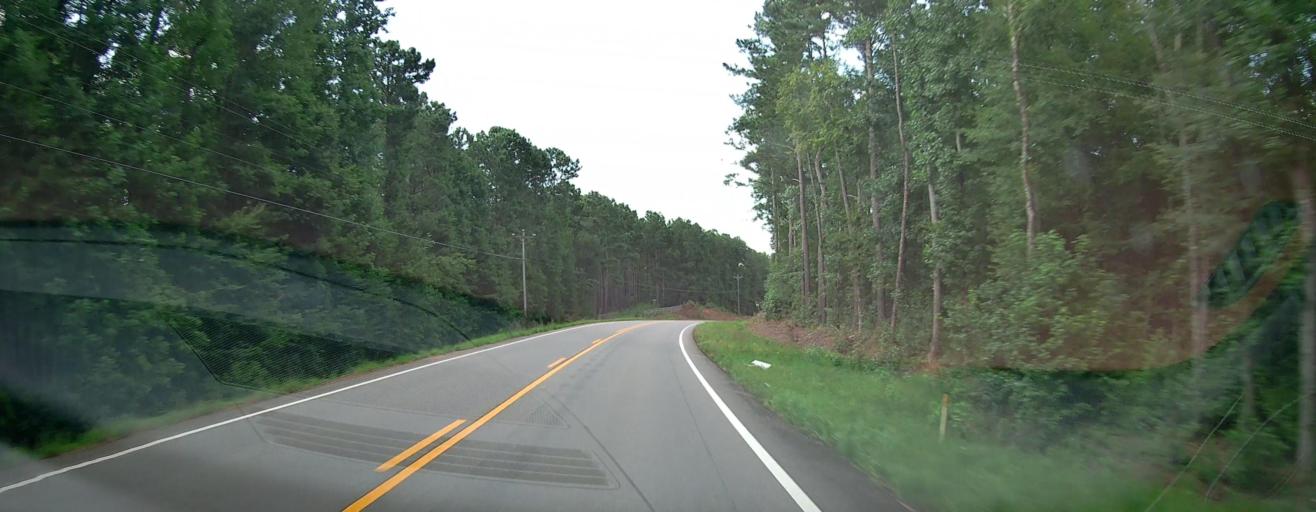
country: US
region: Georgia
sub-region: Monroe County
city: Forsyth
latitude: 32.9889
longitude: -83.9505
